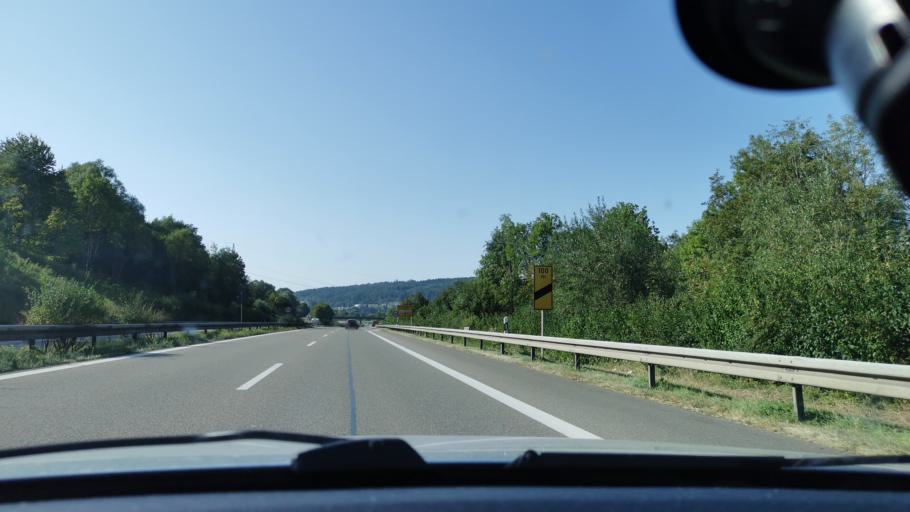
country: DE
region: Baden-Wuerttemberg
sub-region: Regierungsbezirk Stuttgart
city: Albershausen
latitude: 48.7117
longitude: 9.5638
